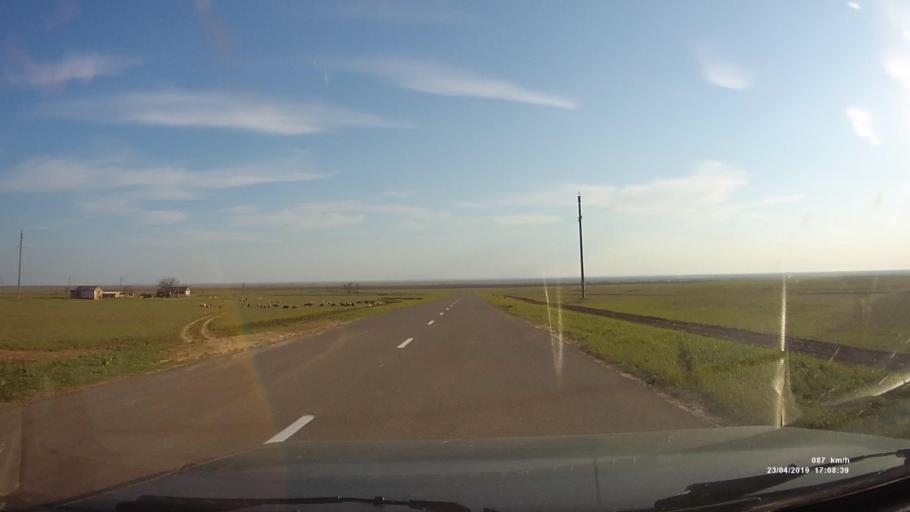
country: RU
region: Kalmykiya
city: Priyutnoye
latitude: 46.2686
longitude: 43.4859
